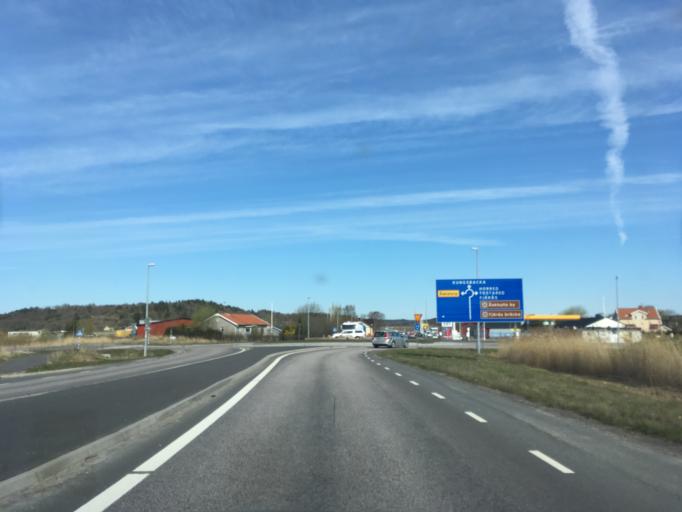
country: SE
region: Halland
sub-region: Kungsbacka Kommun
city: Fjaeras kyrkby
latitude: 57.4345
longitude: 12.1549
